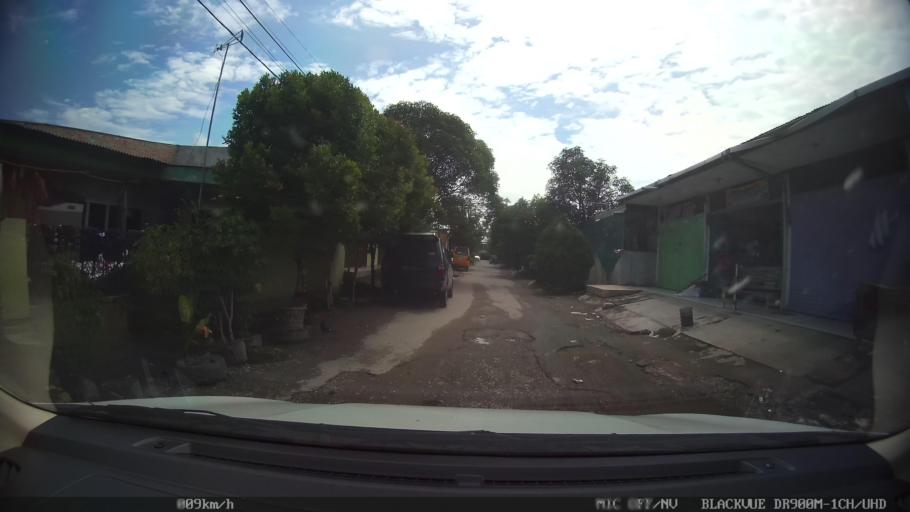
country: ID
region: North Sumatra
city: Medan
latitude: 3.5908
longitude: 98.7377
